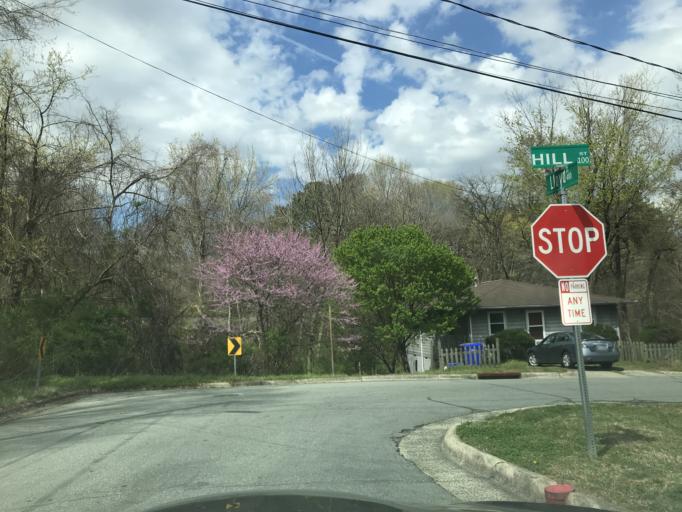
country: US
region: North Carolina
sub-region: Orange County
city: Carrboro
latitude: 35.9149
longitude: -79.0697
